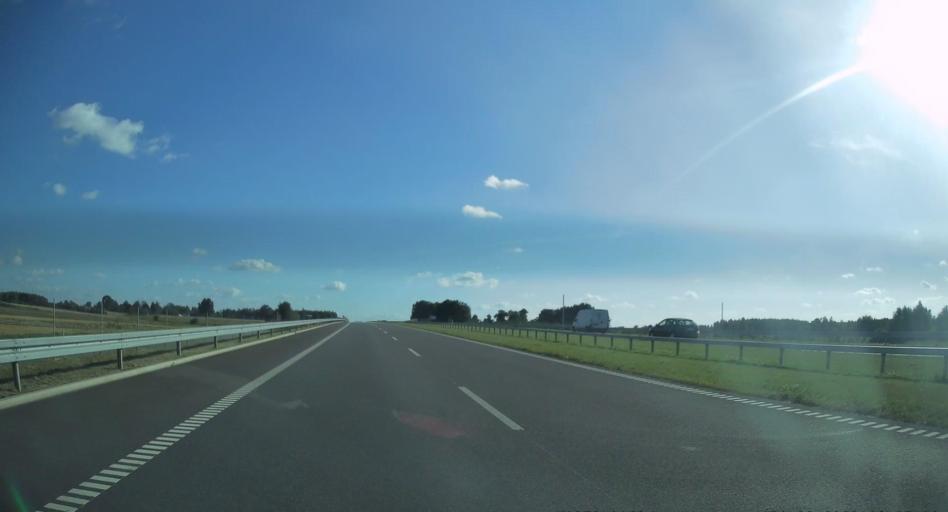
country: PL
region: Masovian Voivodeship
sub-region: Powiat radomski
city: Zakrzew
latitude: 51.4665
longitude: 21.0495
